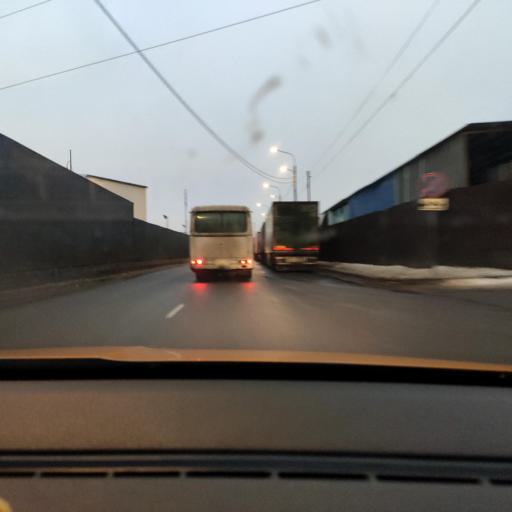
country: RU
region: Moskovskaya
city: Mosrentgen
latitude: 55.6199
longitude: 37.4533
